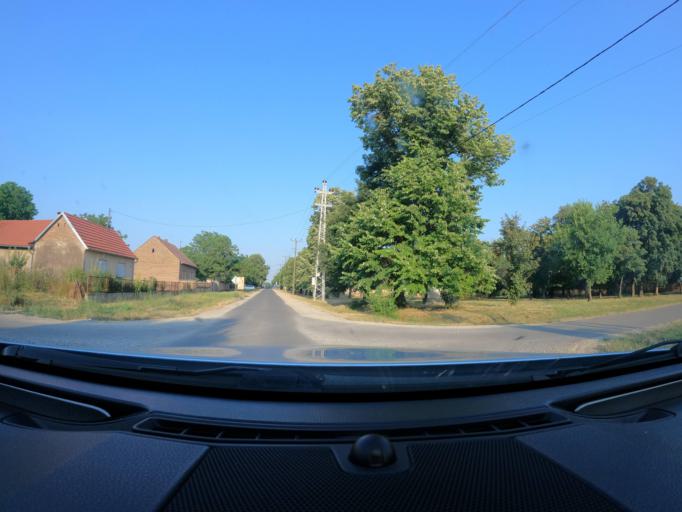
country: RS
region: Autonomna Pokrajina Vojvodina
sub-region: Sremski Okrug
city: Ruma
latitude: 45.0521
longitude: 19.7840
